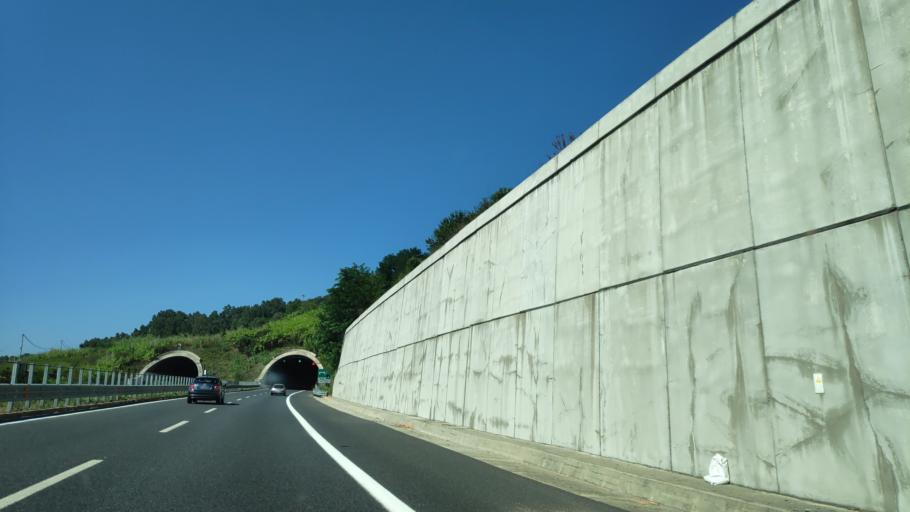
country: IT
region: Calabria
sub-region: Provincia di Reggio Calabria
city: Seminara
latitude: 38.3340
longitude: 15.8597
